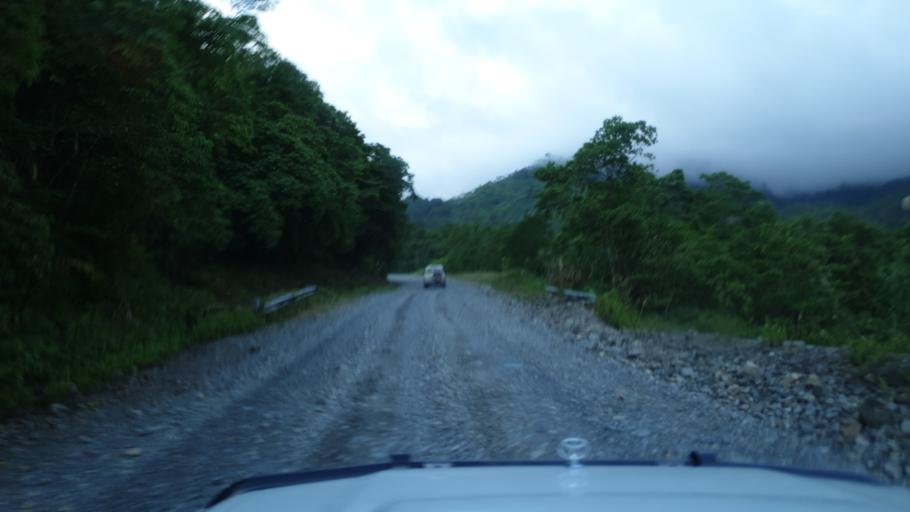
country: PG
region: Bougainville
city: Panguna
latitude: -6.3371
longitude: 155.4610
